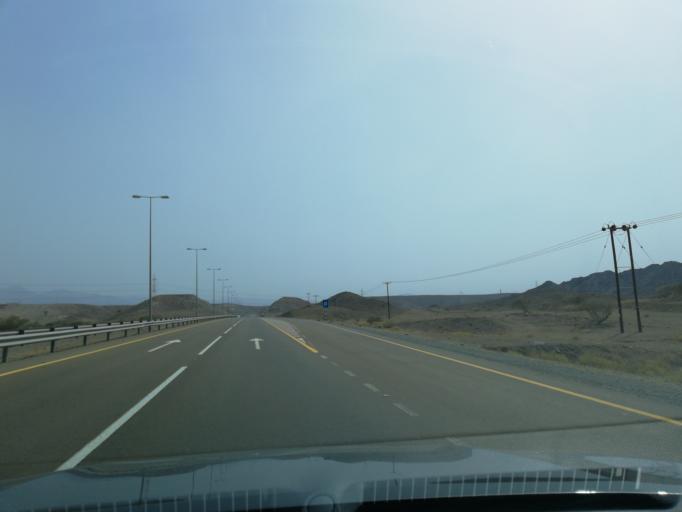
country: OM
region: Al Batinah
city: Al Liwa'
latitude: 24.3159
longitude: 56.4525
